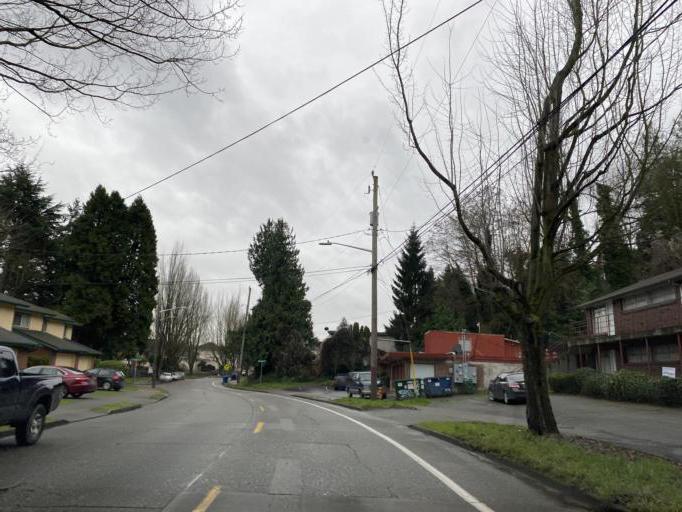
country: US
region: Washington
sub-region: King County
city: Seattle
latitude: 47.5877
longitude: -122.3138
